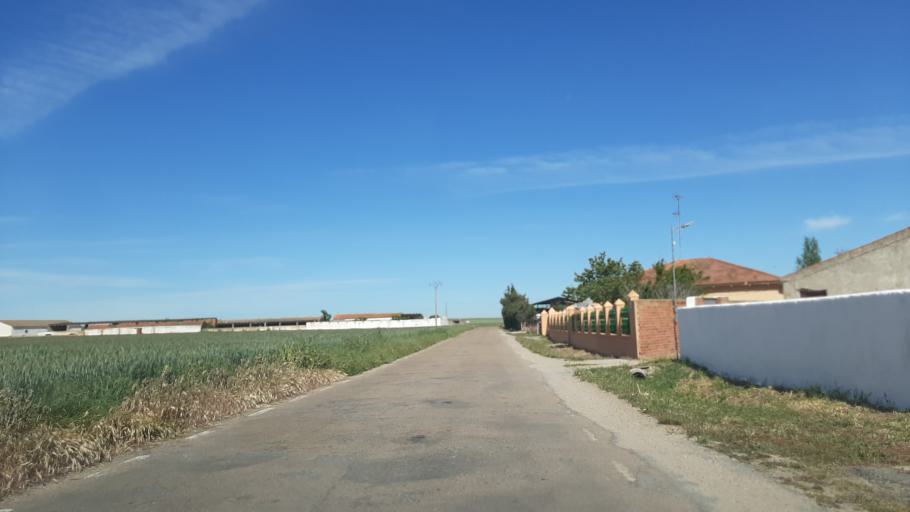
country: ES
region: Castille and Leon
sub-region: Provincia de Salamanca
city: Pedrosillo de Alba
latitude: 40.8200
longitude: -5.3936
